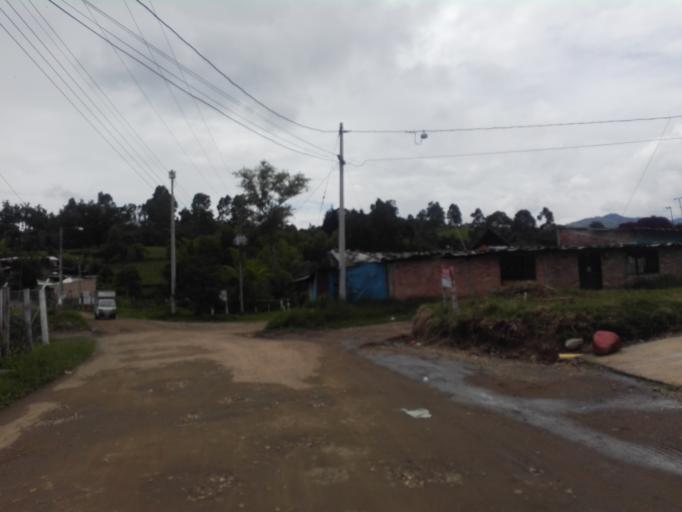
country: CO
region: Cauca
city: Popayan
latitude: 2.3512
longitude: -76.6722
